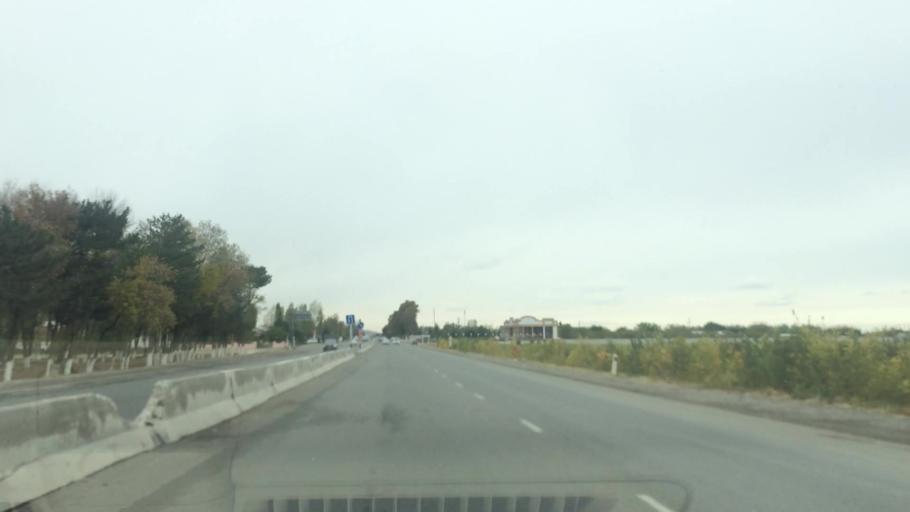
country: UZ
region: Samarqand
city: Jomboy
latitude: 39.7196
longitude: 67.1174
